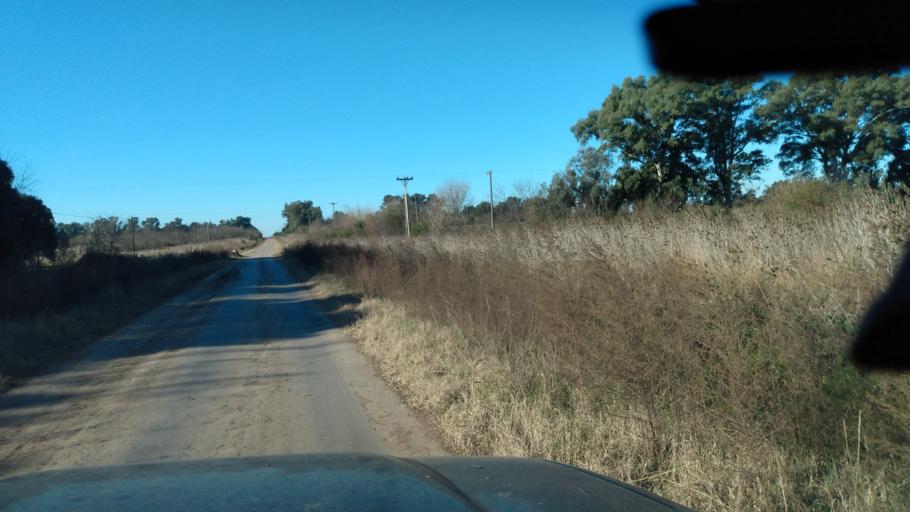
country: AR
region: Buenos Aires
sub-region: Partido de Lujan
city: Lujan
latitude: -34.5633
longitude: -59.1662
